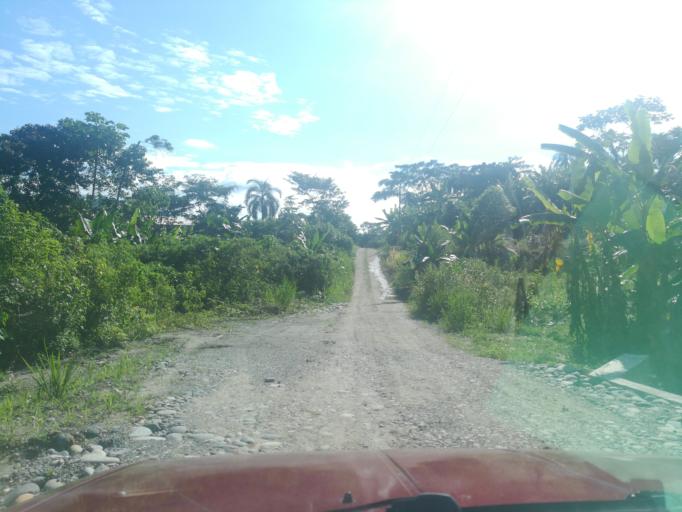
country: EC
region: Napo
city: Tena
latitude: -0.9932
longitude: -77.8341
